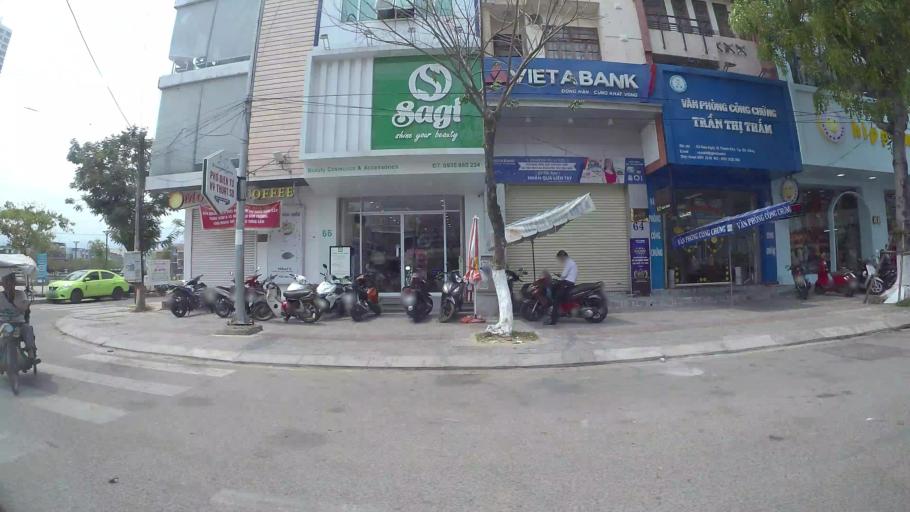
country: VN
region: Da Nang
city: Da Nang
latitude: 16.0647
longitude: 108.2105
